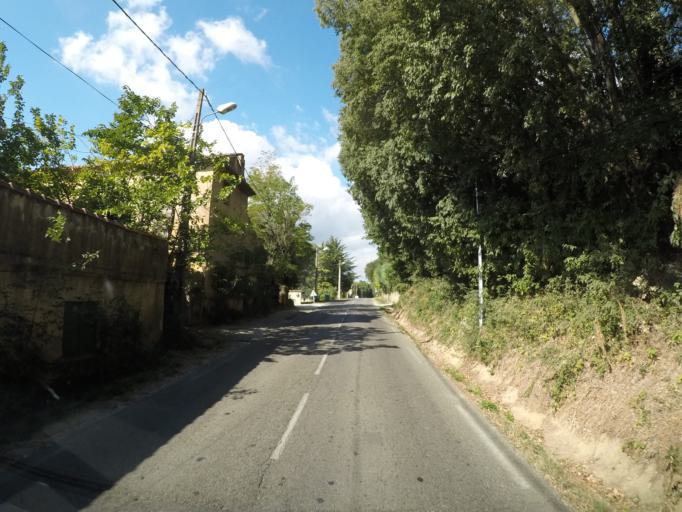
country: FR
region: Rhone-Alpes
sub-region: Departement de la Drome
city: Suze-la-Rousse
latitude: 44.2949
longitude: 4.8356
